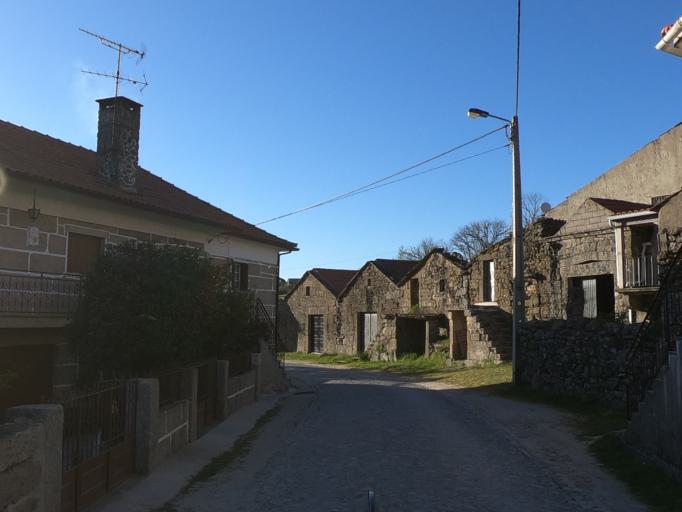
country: PT
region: Vila Real
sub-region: Vila Real
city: Vila Real
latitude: 41.3606
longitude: -7.6510
